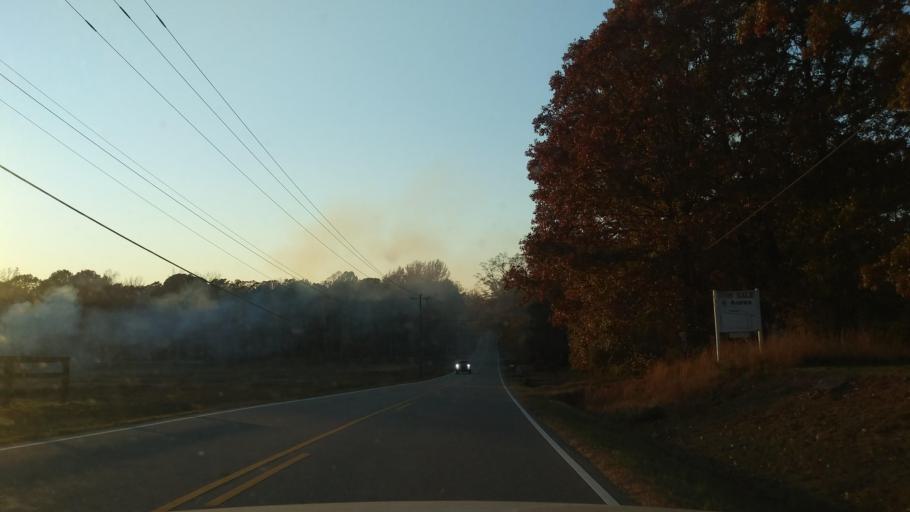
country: US
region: North Carolina
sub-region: Guilford County
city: Pleasant Garden
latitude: 35.9912
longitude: -79.7888
